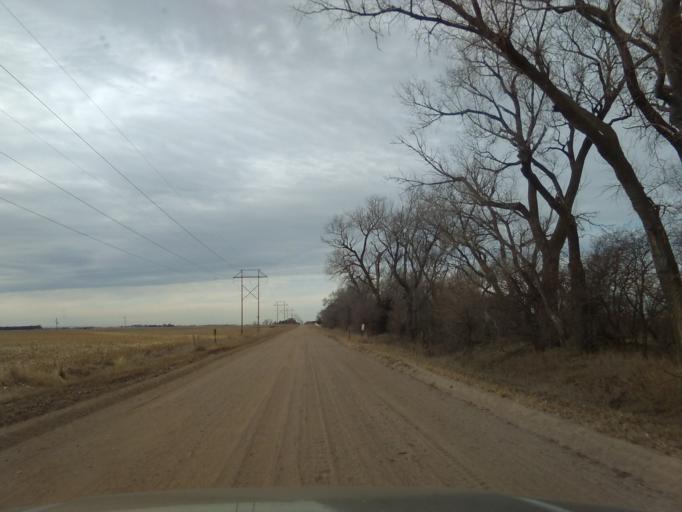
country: US
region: Nebraska
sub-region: Buffalo County
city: Shelton
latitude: 40.6549
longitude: -98.7578
